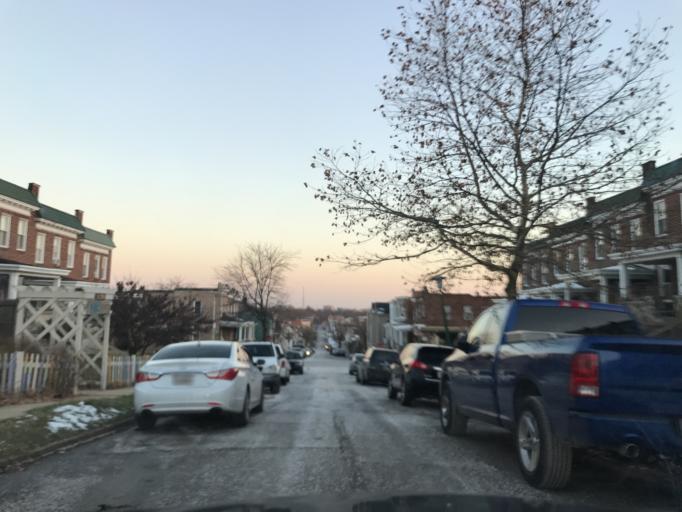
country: US
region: Maryland
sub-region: City of Baltimore
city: Baltimore
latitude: 39.3240
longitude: -76.5972
